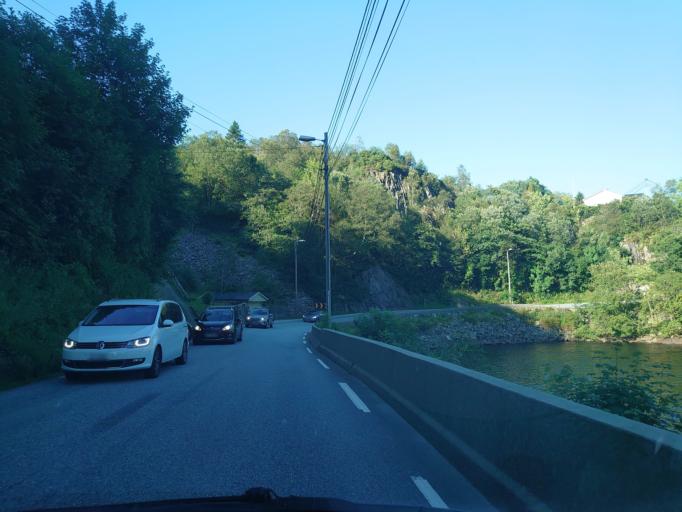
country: NO
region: Hordaland
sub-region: Bergen
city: Espeland
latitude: 60.3504
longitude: 5.4250
